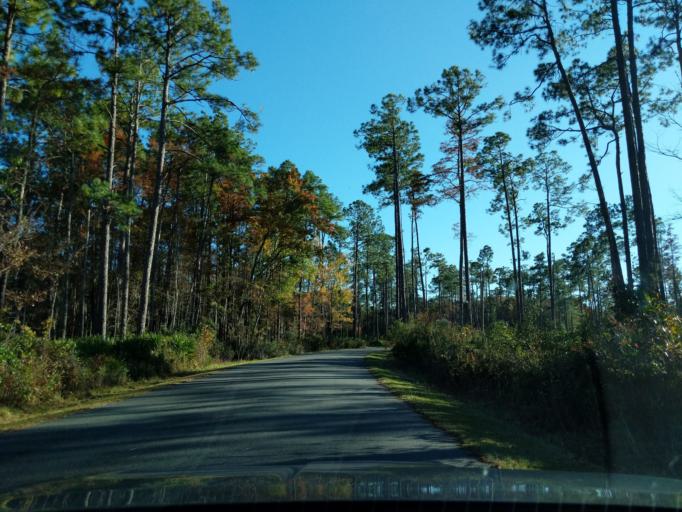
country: US
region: Georgia
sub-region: Charlton County
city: Folkston
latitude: 30.7153
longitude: -82.1408
